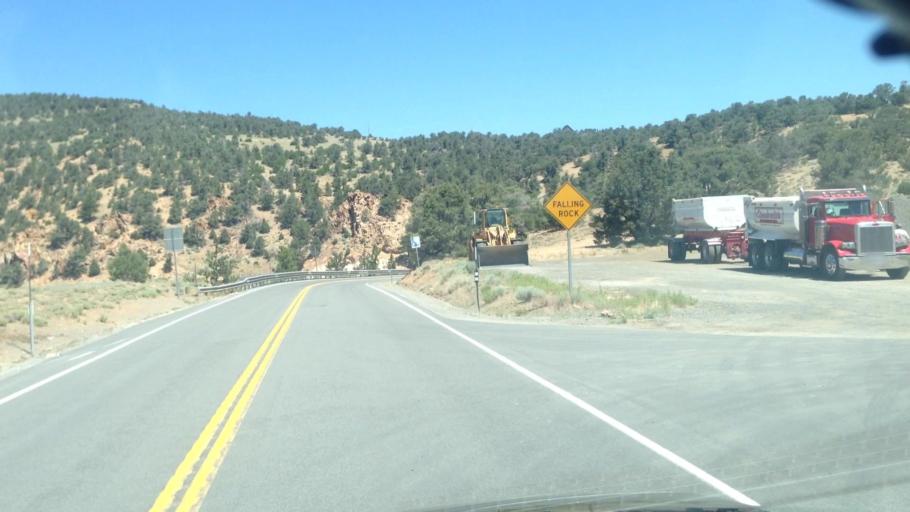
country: US
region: Nevada
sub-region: Storey County
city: Virginia City
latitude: 39.3705
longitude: -119.6675
